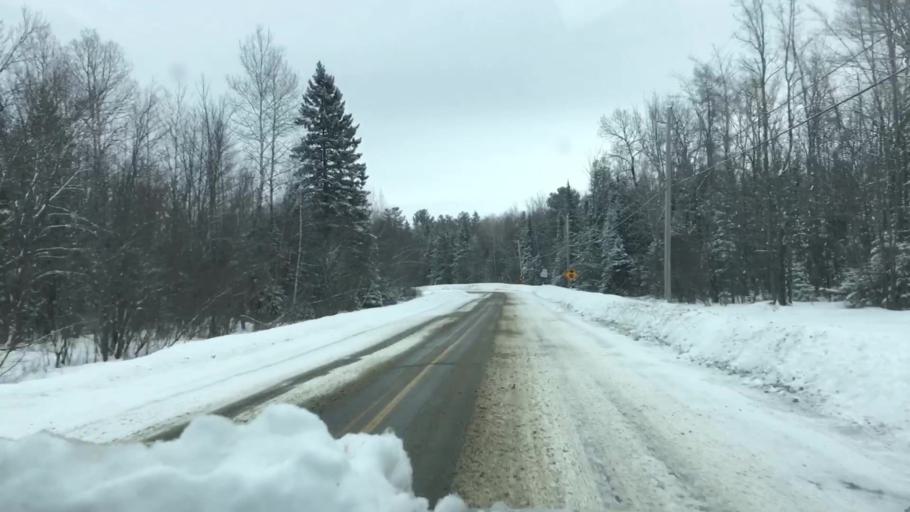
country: US
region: Maine
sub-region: Penobscot County
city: Hudson
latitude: 45.0221
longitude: -68.9166
